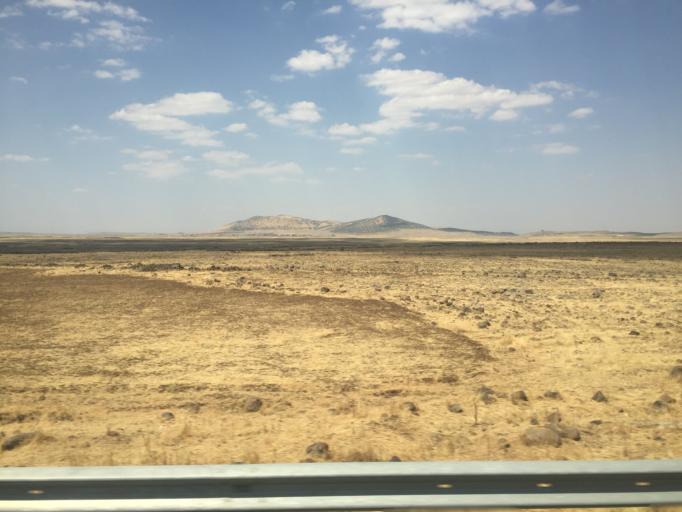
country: TR
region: Sanliurfa
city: Karacadag
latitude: 37.8466
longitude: 39.7090
